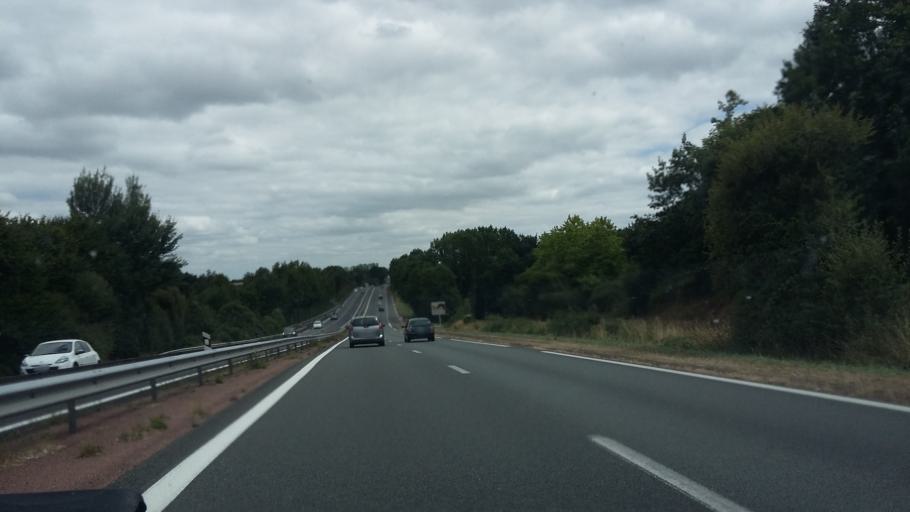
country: FR
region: Pays de la Loire
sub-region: Departement de la Vendee
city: Mouilleron-le-Captif
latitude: 46.6891
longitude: -1.4630
